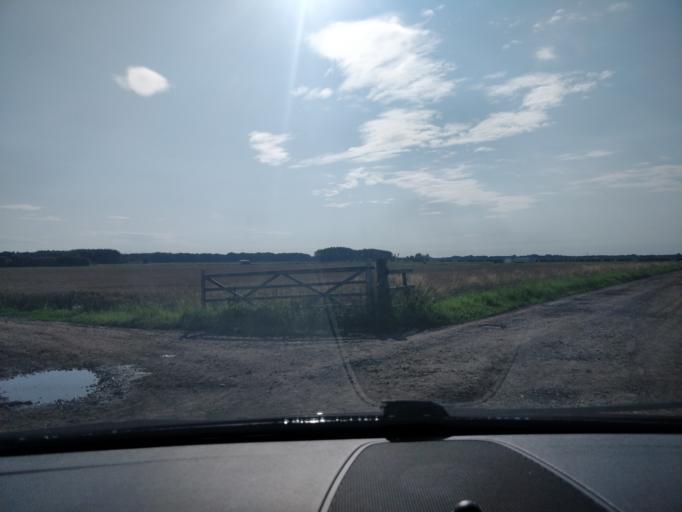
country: GB
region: England
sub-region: Lancashire
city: Banks
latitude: 53.6478
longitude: -2.9052
